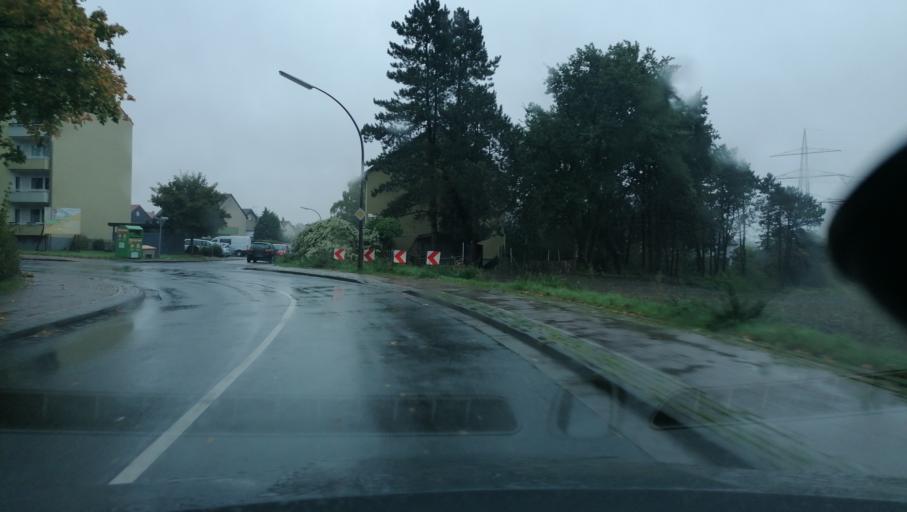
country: DE
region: North Rhine-Westphalia
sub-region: Regierungsbezirk Arnsberg
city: Herne
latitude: 51.5838
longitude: 7.2533
